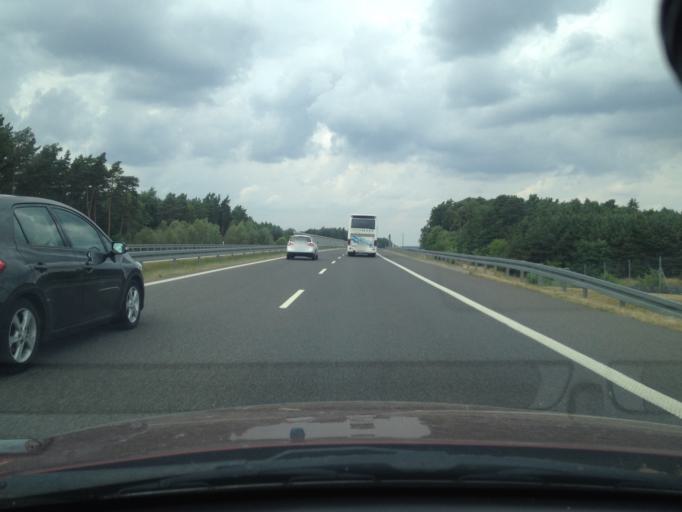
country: PL
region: West Pomeranian Voivodeship
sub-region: Powiat pyrzycki
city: Lipiany
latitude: 52.9614
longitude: 14.9250
